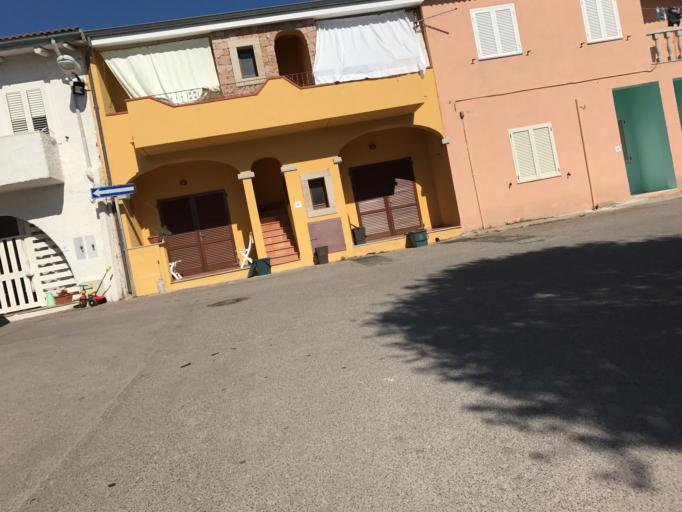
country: IT
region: Sardinia
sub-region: Provincia di Olbia-Tempio
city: Trinita d'Agultu
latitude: 41.0122
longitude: 8.8779
